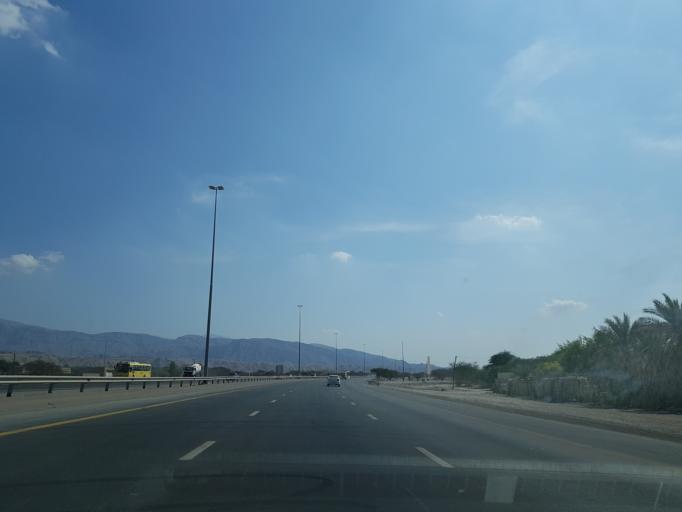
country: AE
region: Ra's al Khaymah
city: Ras al-Khaimah
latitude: 25.8101
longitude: 56.0294
